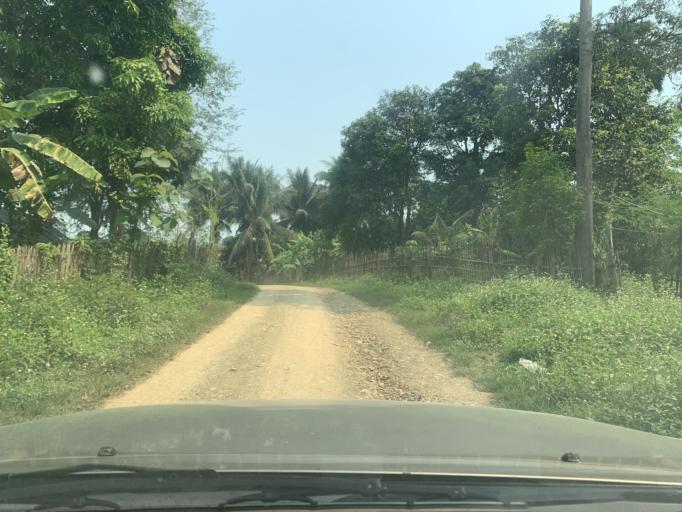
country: LA
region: Louangphabang
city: Xiang Ngeun
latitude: 19.8014
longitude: 102.2045
